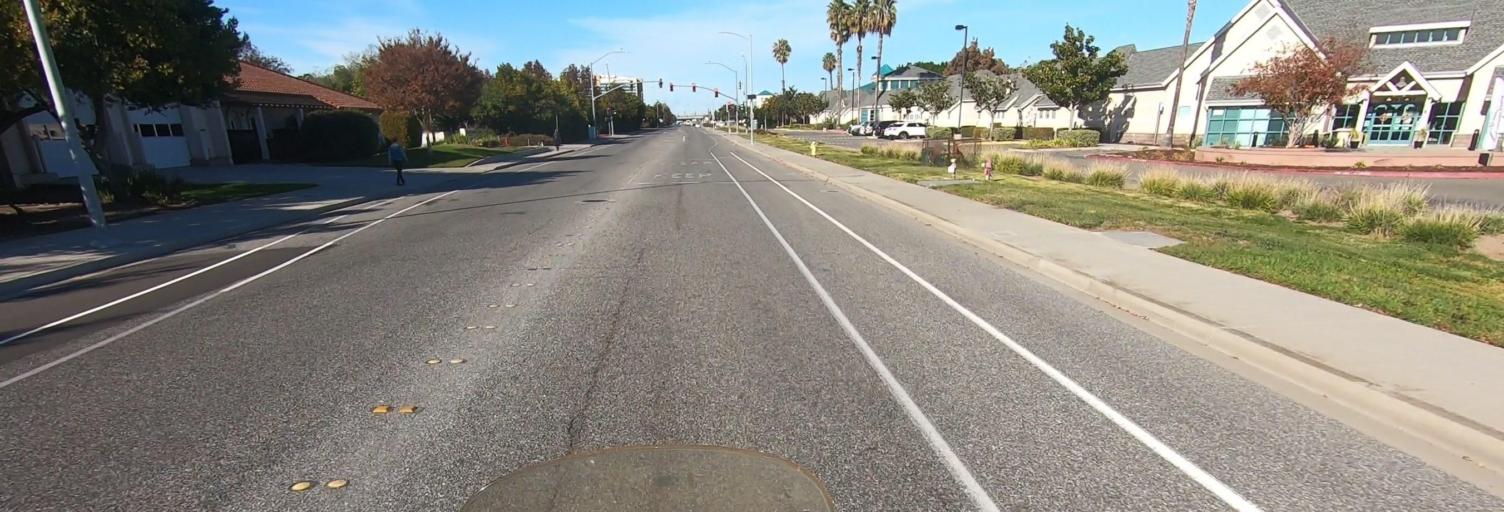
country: US
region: California
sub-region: Santa Clara County
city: Milpitas
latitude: 37.4143
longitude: -121.9082
